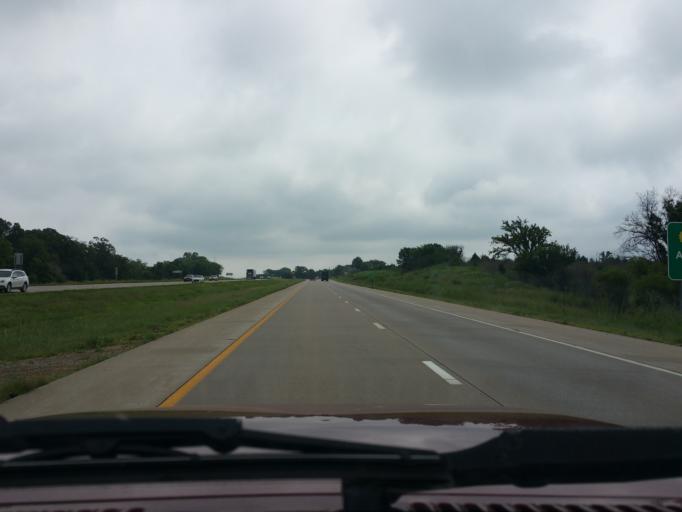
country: US
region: Kansas
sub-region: Shawnee County
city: Silver Lake
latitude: 39.0543
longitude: -95.8375
